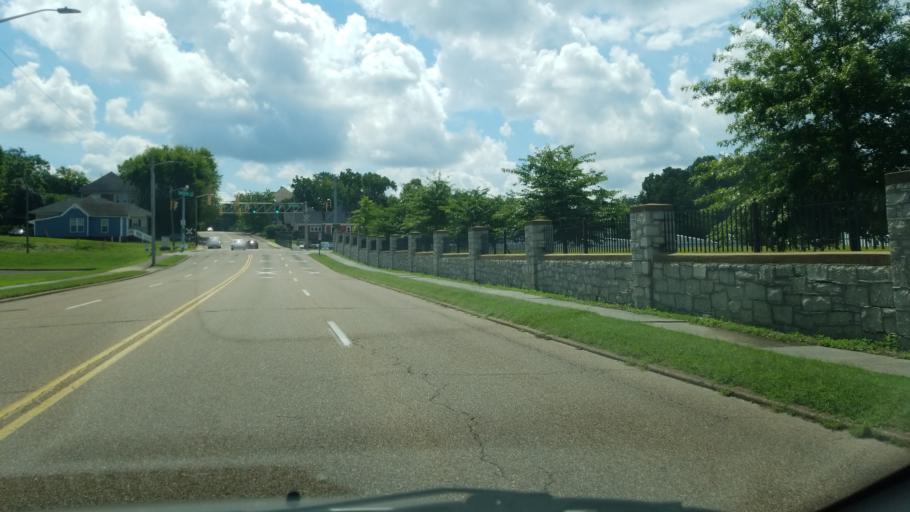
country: US
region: Tennessee
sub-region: Hamilton County
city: Chattanooga
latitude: 35.0369
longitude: -85.2851
